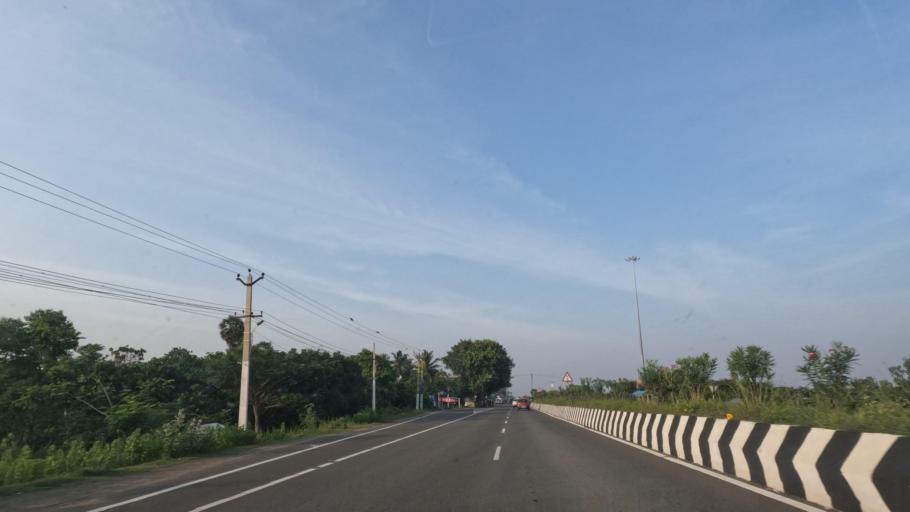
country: IN
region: Tamil Nadu
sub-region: Kancheepuram
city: Mamallapuram
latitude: 12.6882
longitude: 80.2168
